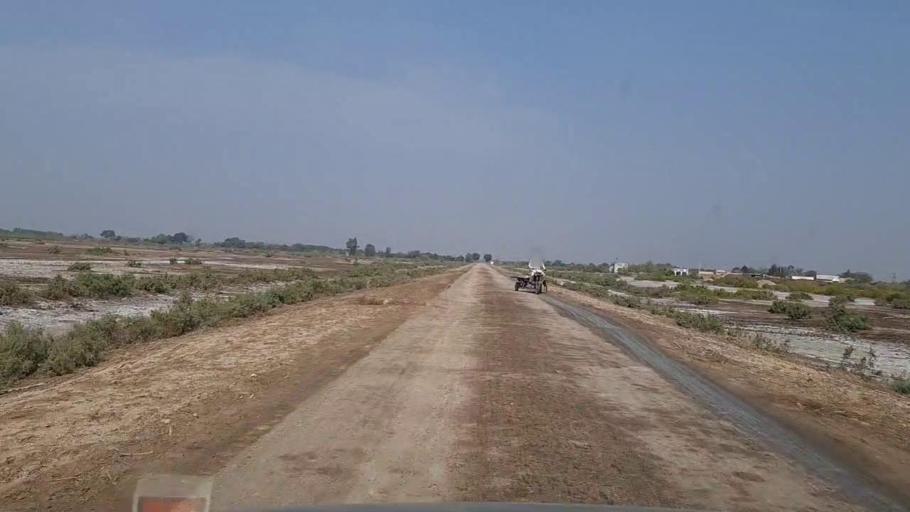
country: PK
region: Sindh
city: Mirwah Gorchani
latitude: 25.3228
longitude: 69.0615
